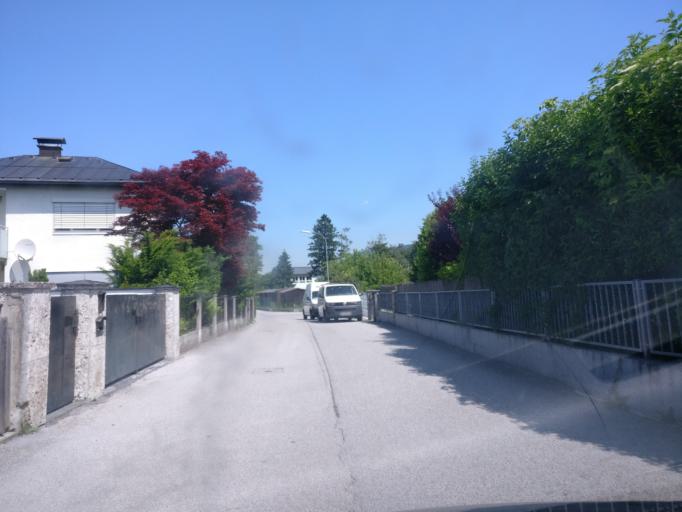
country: AT
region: Salzburg
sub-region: Politischer Bezirk Hallein
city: Oberalm
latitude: 47.6962
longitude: 13.0979
